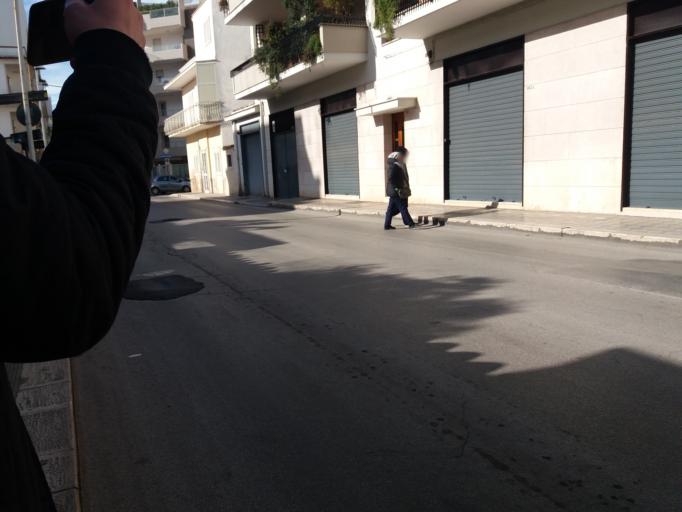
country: IT
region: Apulia
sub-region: Provincia di Bari
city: Bitonto
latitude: 41.1124
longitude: 16.6856
